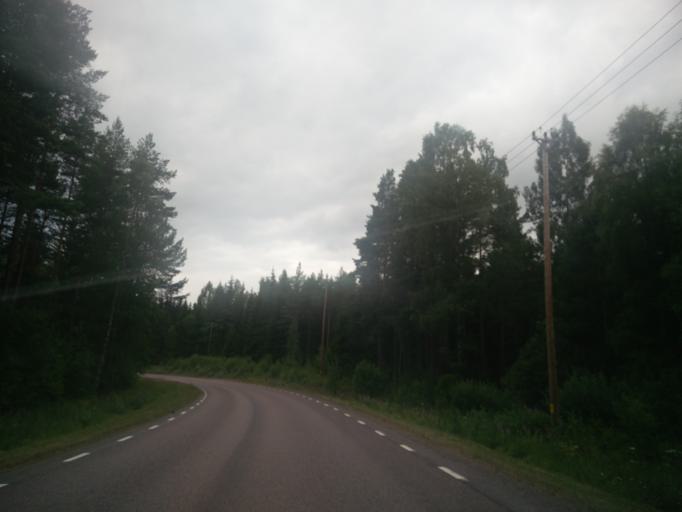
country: SE
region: Vaermland
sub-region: Arvika Kommun
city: Arvika
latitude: 59.9563
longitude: 12.7181
